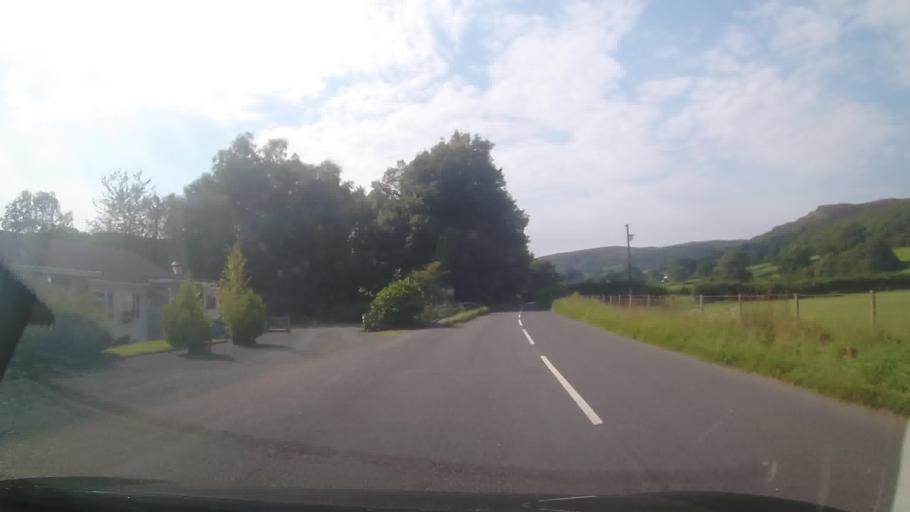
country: GB
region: Wales
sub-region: Sir Powys
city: Rhayader
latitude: 52.2891
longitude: -3.5361
